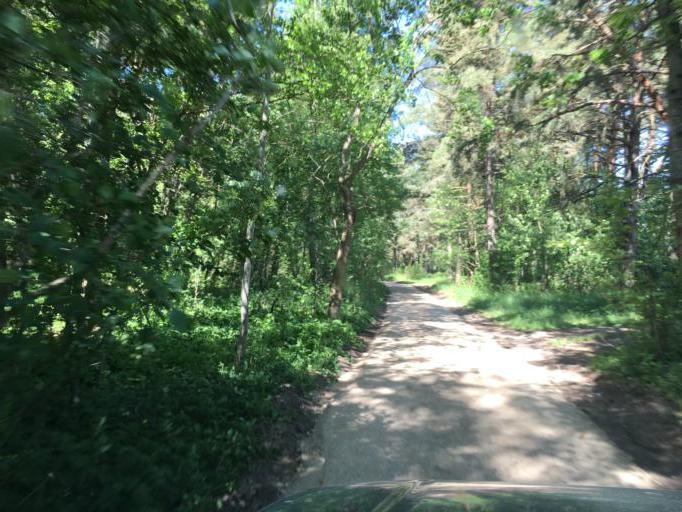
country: LV
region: Ventspils
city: Ventspils
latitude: 57.4585
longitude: 21.6474
